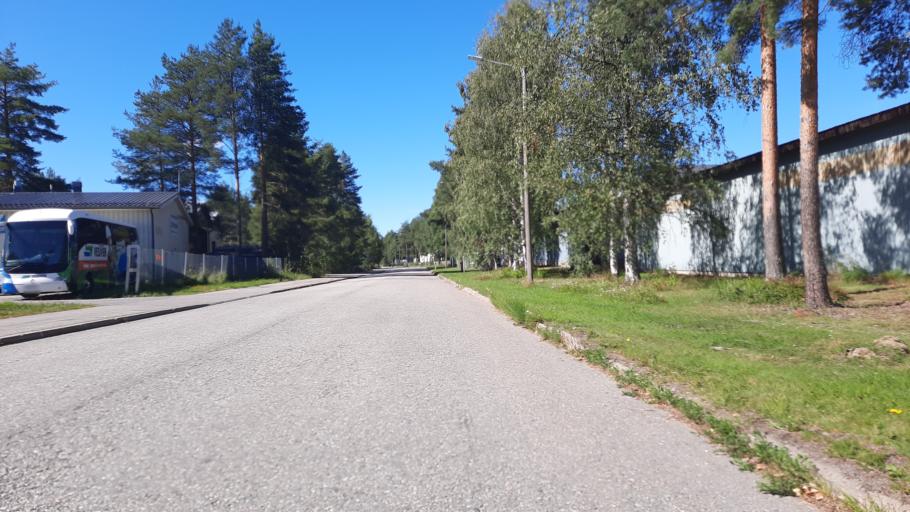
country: FI
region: North Karelia
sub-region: Joensuu
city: Joensuu
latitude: 62.6240
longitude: 29.7464
